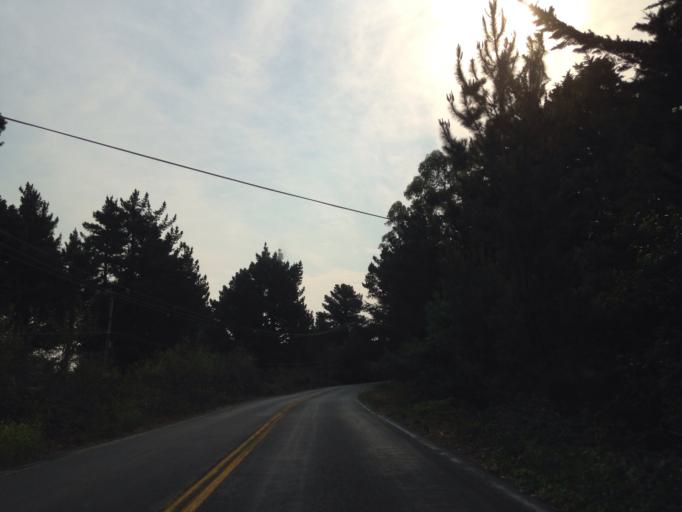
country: US
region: California
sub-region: San Mateo County
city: Highlands-Baywood Park
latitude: 37.4697
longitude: -122.3527
